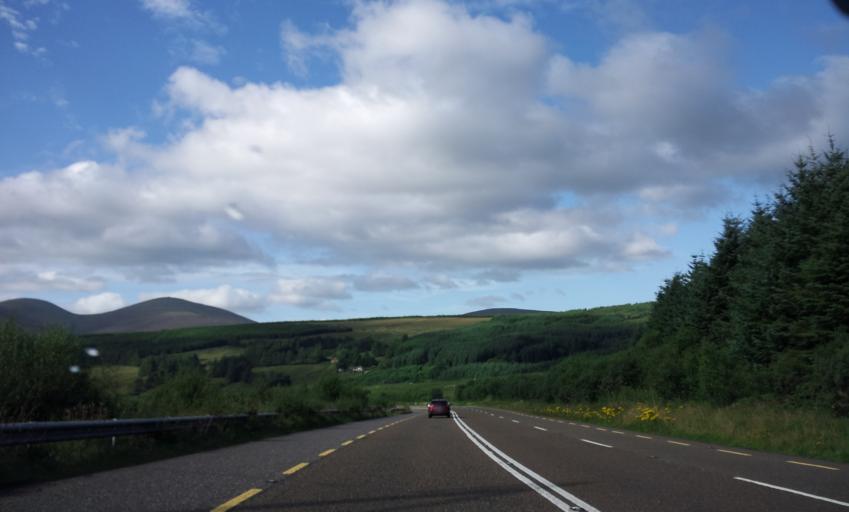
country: IE
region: Munster
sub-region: County Cork
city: Millstreet
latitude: 51.9733
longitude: -9.2527
